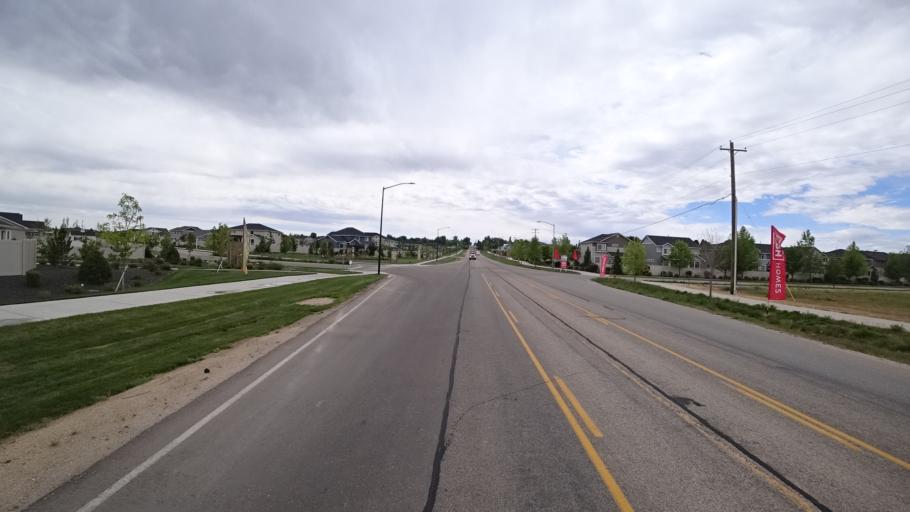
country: US
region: Idaho
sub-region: Ada County
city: Meridian
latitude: 43.5869
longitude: -116.4137
